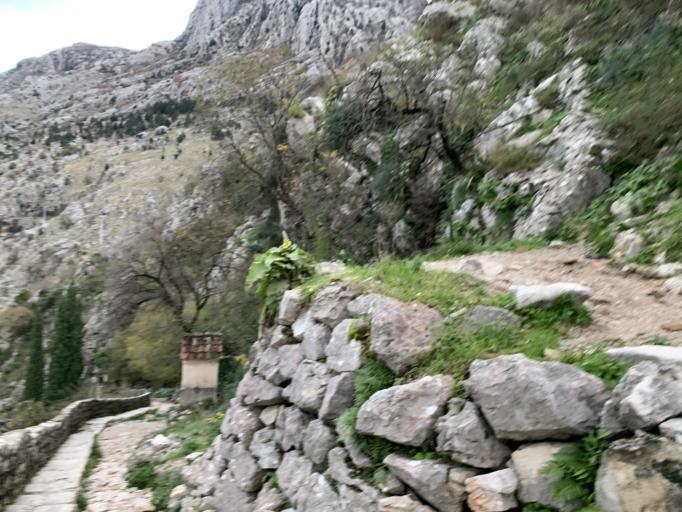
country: ME
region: Kotor
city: Kotor
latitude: 42.4244
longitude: 18.7732
